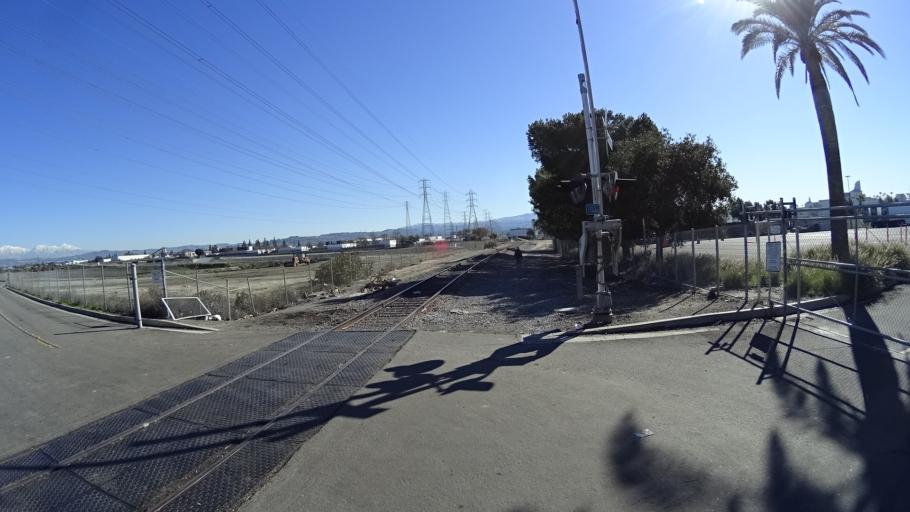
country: US
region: California
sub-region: Orange County
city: Orange
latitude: 33.8121
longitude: -117.8737
